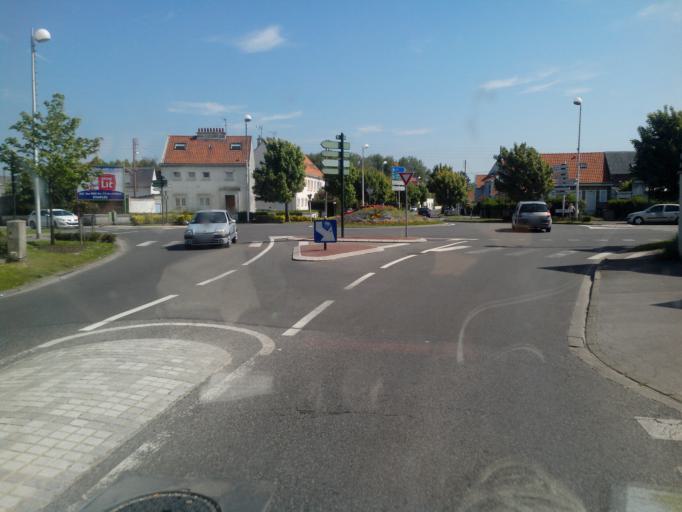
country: FR
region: Nord-Pas-de-Calais
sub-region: Departement du Pas-de-Calais
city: Berck
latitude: 50.4091
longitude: 1.5946
